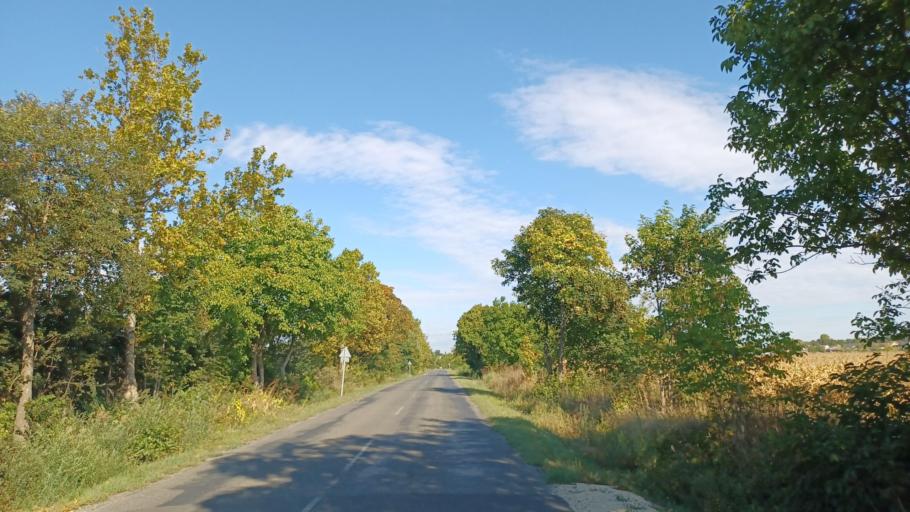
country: HU
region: Tolna
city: Dunaszentgyorgy
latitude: 46.5184
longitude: 18.8273
